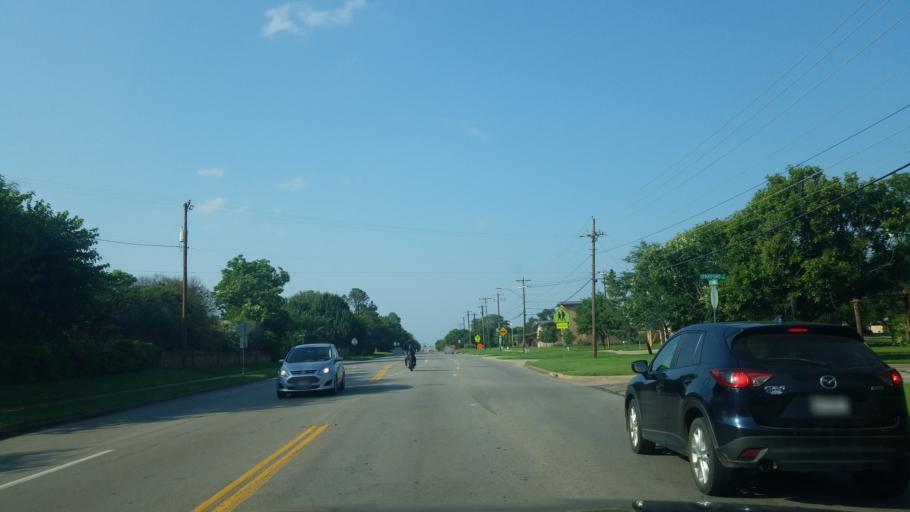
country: US
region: Texas
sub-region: Denton County
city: Denton
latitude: 33.2485
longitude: -97.1162
